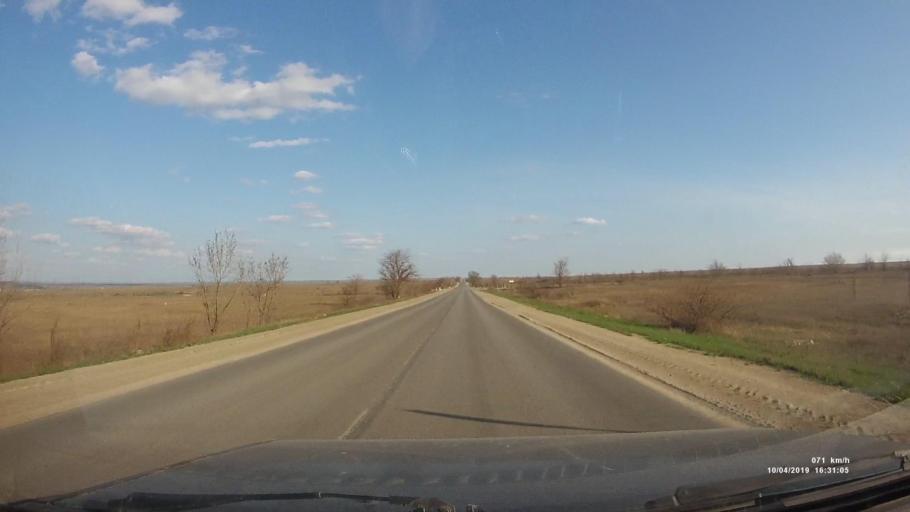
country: RU
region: Rostov
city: Staraya Stanitsa
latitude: 48.2570
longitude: 40.3722
